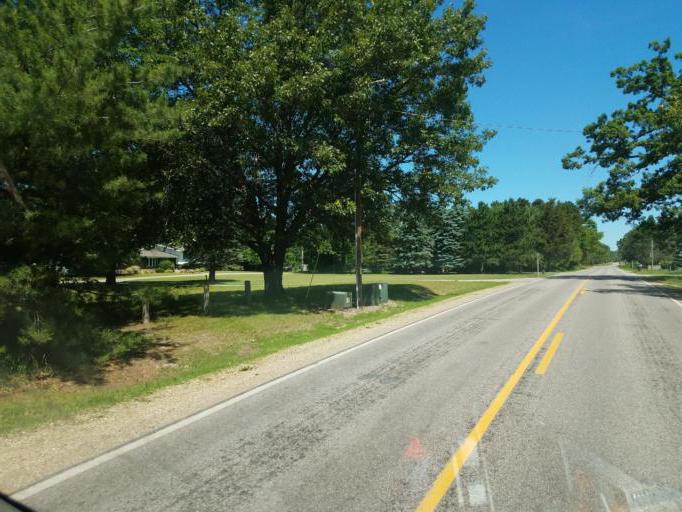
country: US
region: Wisconsin
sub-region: Adams County
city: Adams
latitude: 43.9103
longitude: -89.9378
